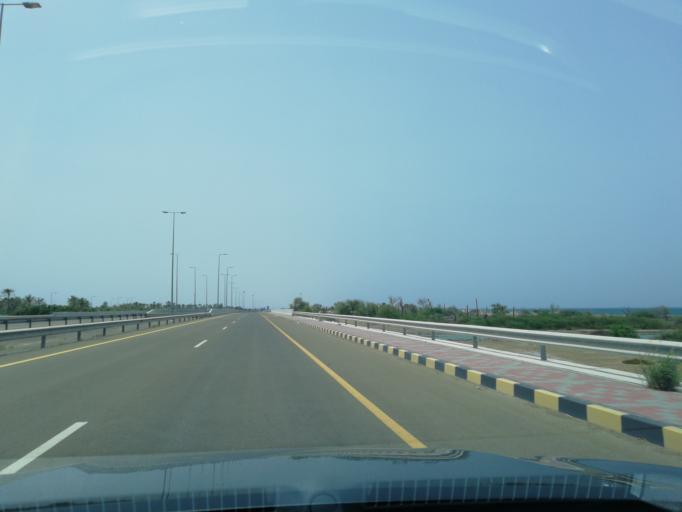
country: OM
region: Al Batinah
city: Al Liwa'
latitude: 24.6368
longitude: 56.5235
